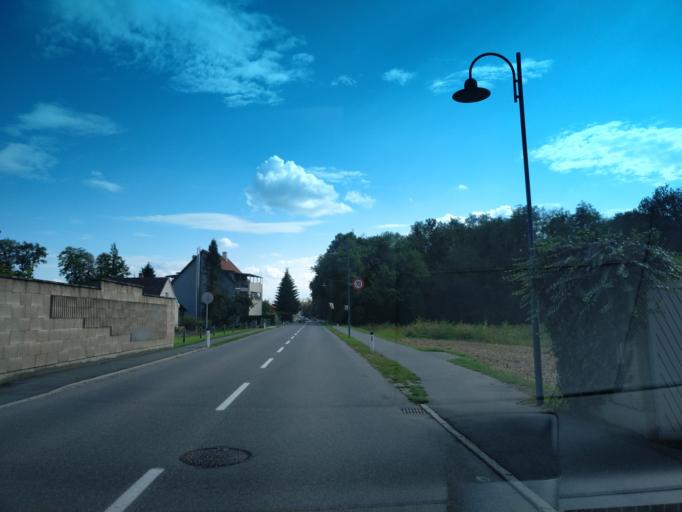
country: AT
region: Styria
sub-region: Politischer Bezirk Leibnitz
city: Kaindorf an der Sulm
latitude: 46.7899
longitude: 15.5334
